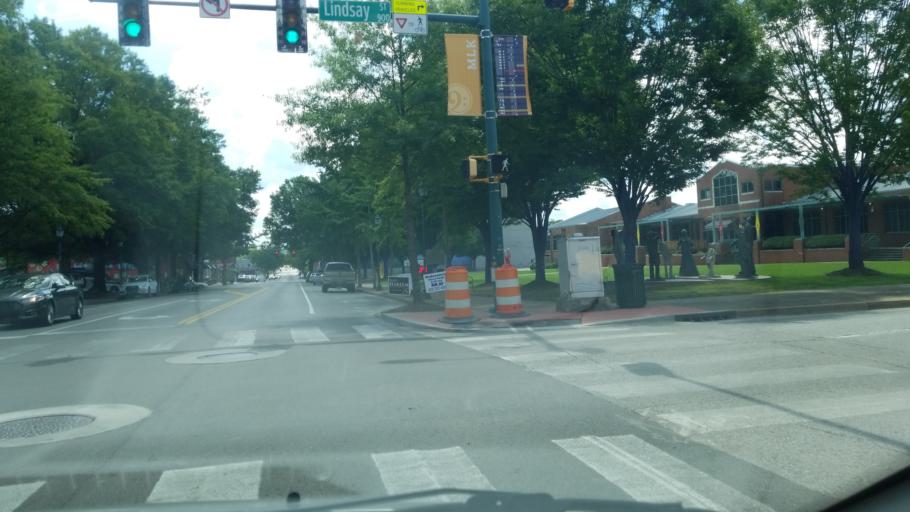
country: US
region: Tennessee
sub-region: Hamilton County
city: Chattanooga
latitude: 35.0453
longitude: -85.3071
